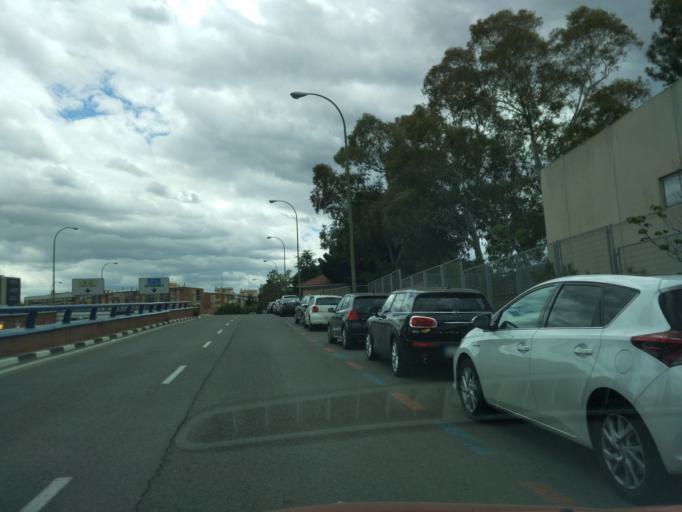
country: ES
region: Madrid
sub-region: Provincia de Madrid
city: Chamartin
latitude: 40.4768
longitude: -3.6906
